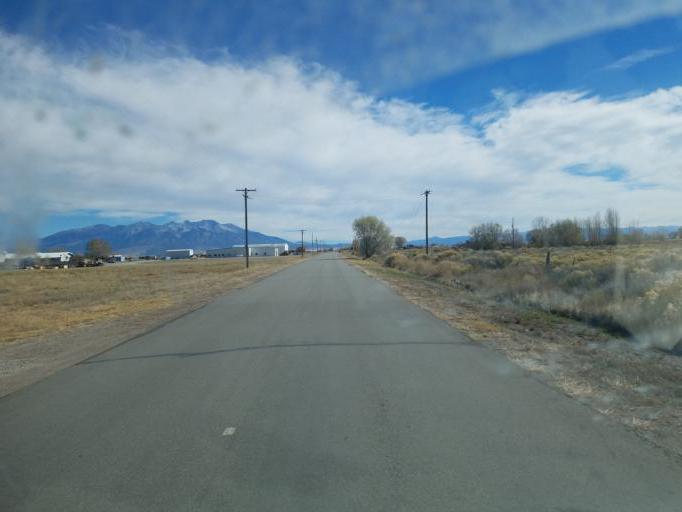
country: US
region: Colorado
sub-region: Alamosa County
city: Alamosa East
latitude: 37.5027
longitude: -105.8207
